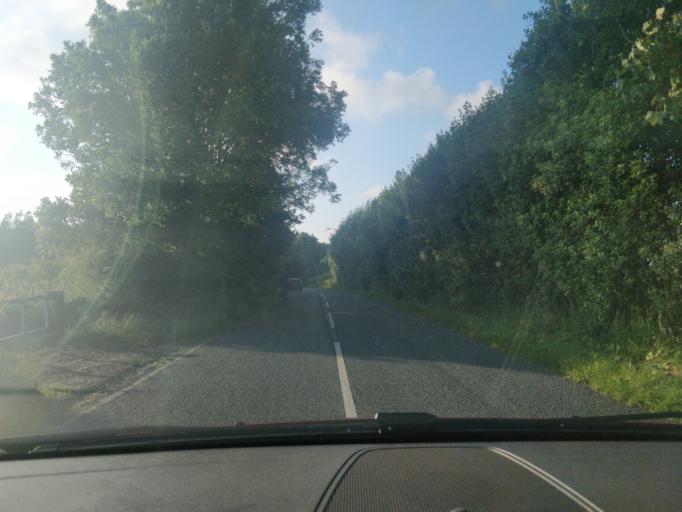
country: GB
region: England
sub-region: Lancashire
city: Skelmersdale
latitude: 53.5539
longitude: -2.7445
